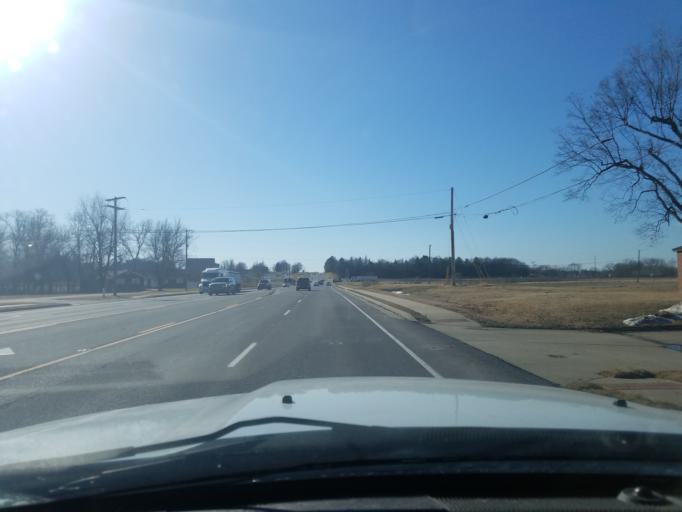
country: US
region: Kentucky
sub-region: Henderson County
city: Henderson
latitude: 37.8014
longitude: -87.6439
